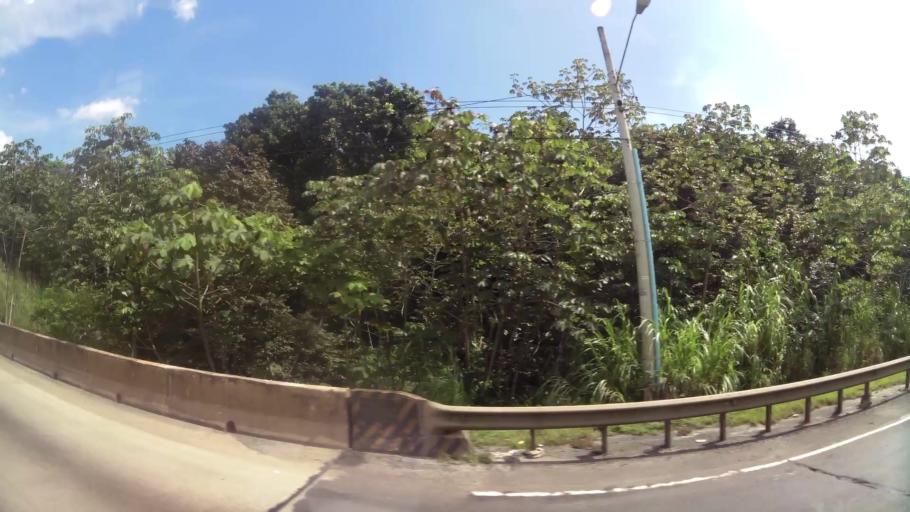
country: PA
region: Panama
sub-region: Distrito de Panama
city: Paraiso
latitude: 9.0360
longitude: -79.5764
